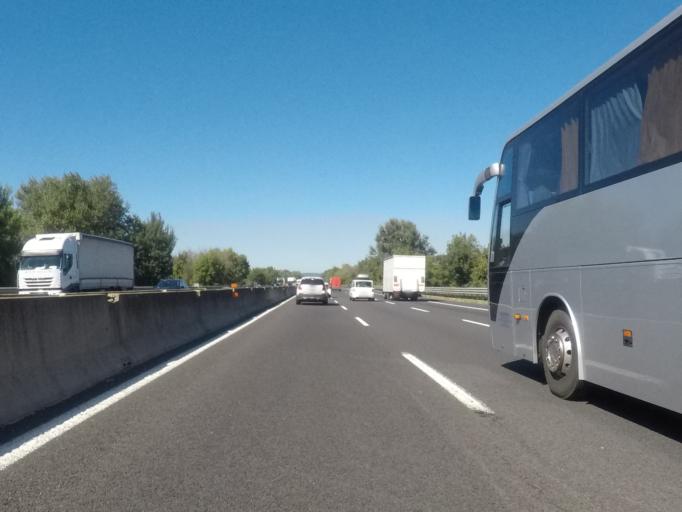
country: IT
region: Umbria
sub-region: Provincia di Terni
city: Otricoli
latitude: 42.4034
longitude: 12.4547
